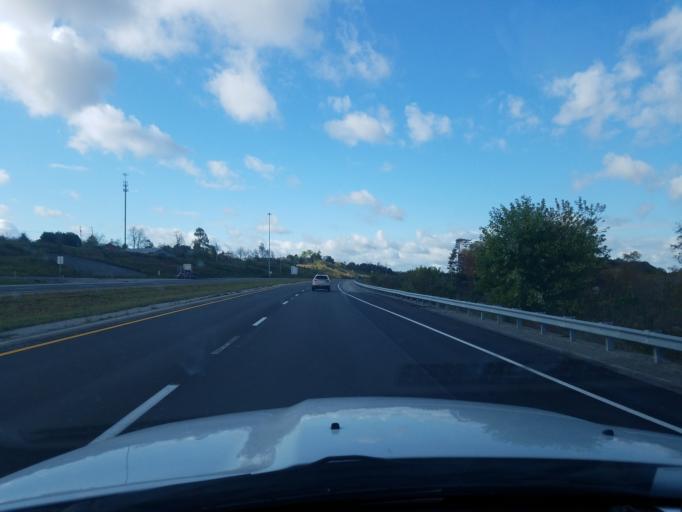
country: US
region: Kentucky
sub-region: Pulaski County
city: Somerset
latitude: 37.1040
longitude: -84.6638
